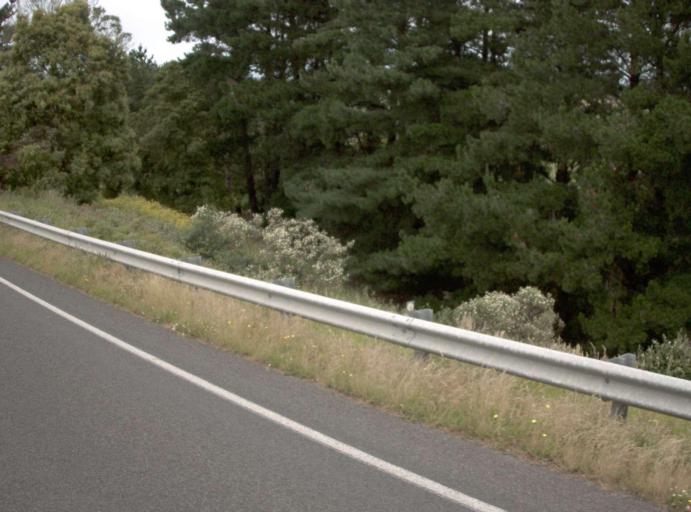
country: AU
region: Victoria
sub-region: Latrobe
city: Morwell
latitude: -38.6301
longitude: 146.1856
